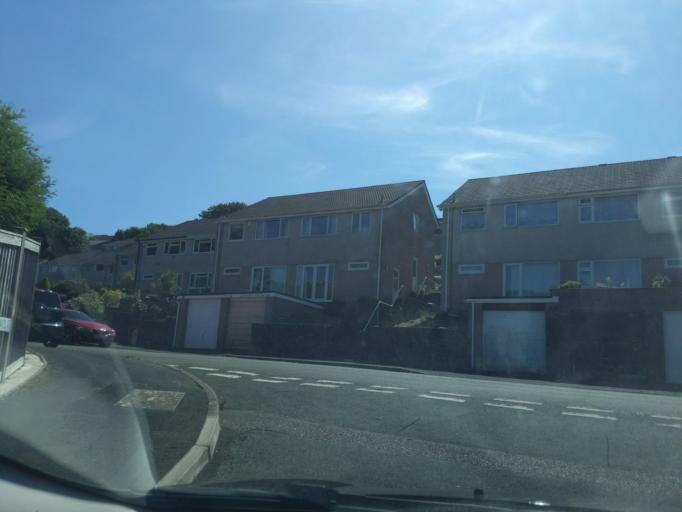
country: GB
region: England
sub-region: Plymouth
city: Plymouth
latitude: 50.4238
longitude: -4.1643
